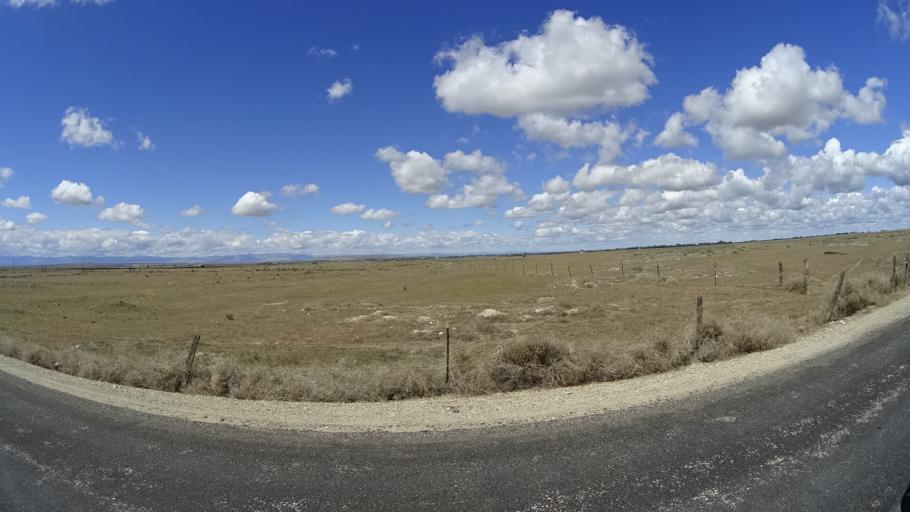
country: US
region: Idaho
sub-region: Ada County
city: Kuna
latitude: 43.4626
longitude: -116.2744
